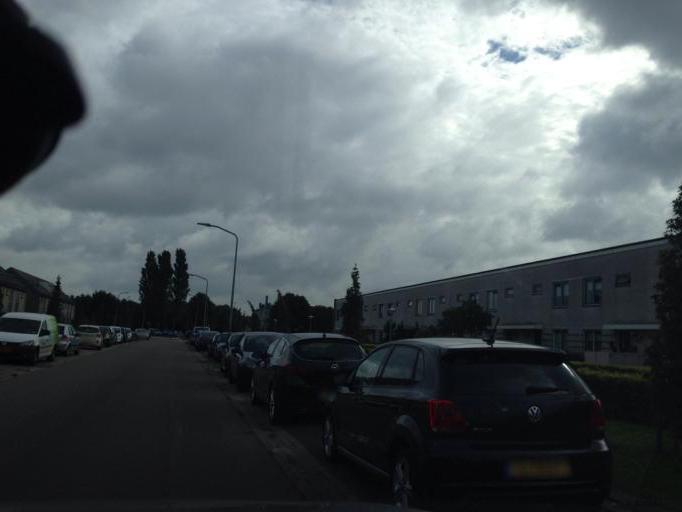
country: NL
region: Flevoland
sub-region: Gemeente Almere
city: Almere Stad
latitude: 52.3697
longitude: 5.1910
